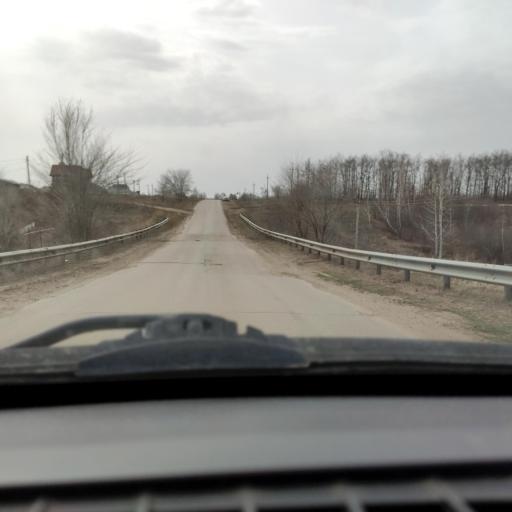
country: RU
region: Samara
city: Dubovyy Umet
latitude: 53.0422
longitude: 50.1778
